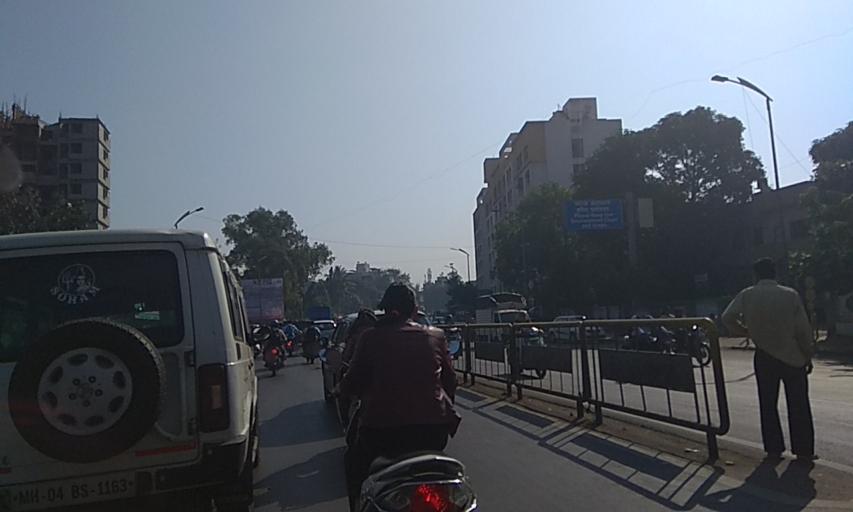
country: IN
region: Maharashtra
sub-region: Pune Division
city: Pune
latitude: 18.5013
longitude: 73.8465
